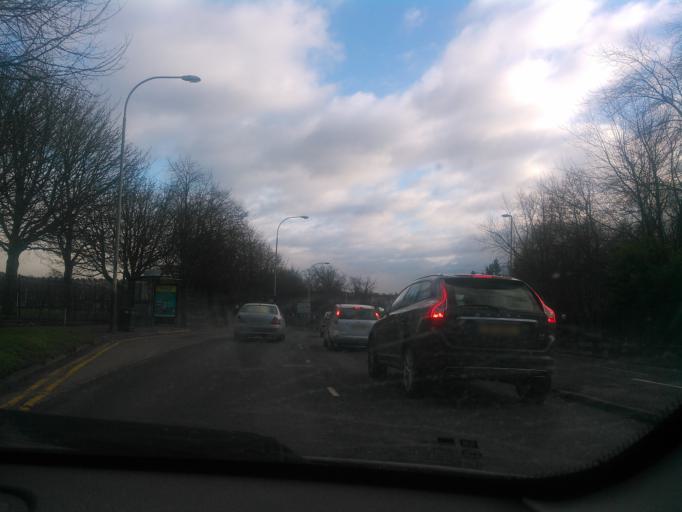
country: GB
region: England
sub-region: City of Leicester
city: Leicester
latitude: 52.6187
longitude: -1.1277
